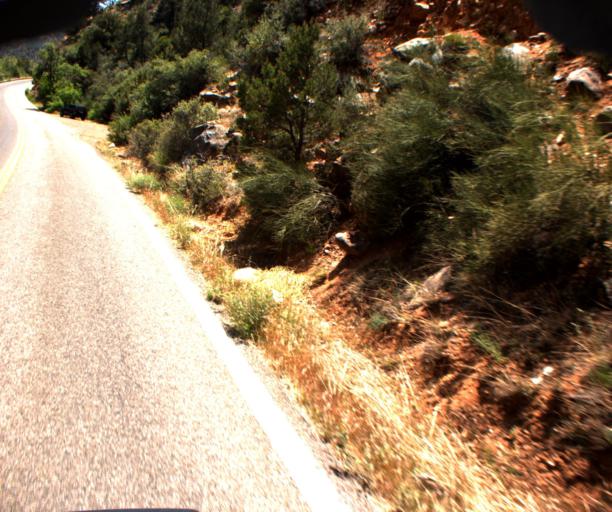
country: US
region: Arizona
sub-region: Coconino County
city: Sedona
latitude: 34.8988
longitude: -111.7318
